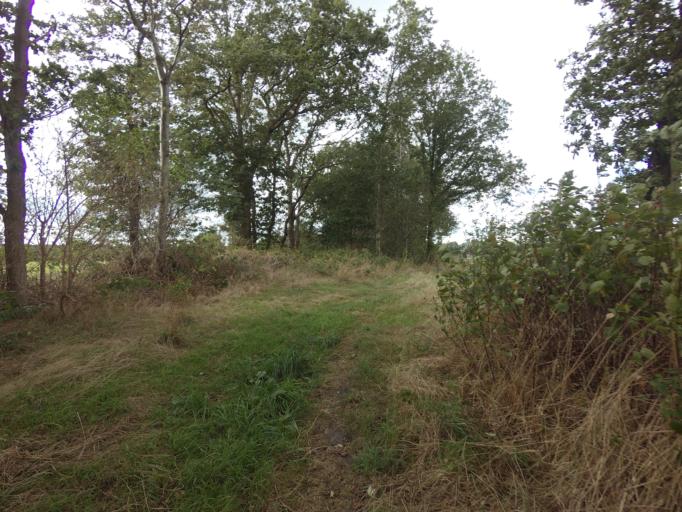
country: NL
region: Friesland
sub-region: Gemeente Heerenveen
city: Jubbega
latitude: 52.9625
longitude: 6.1840
